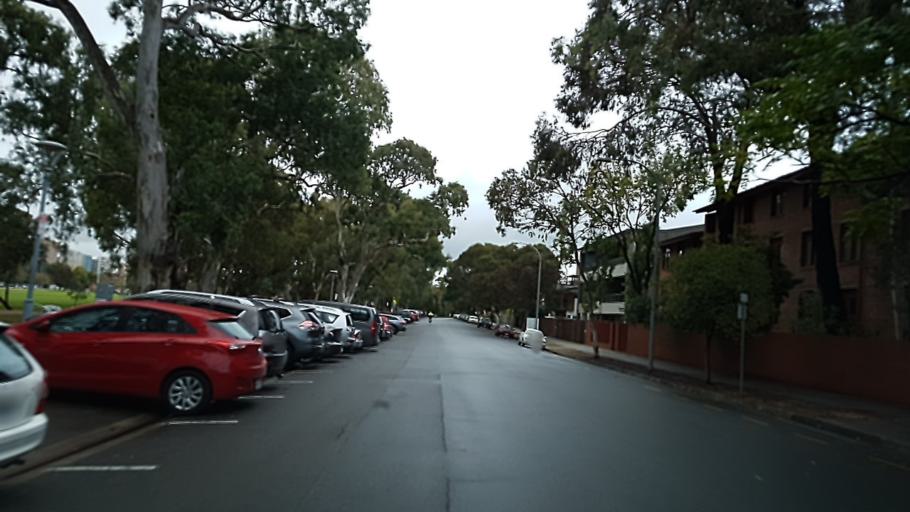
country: AU
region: South Australia
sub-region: Adelaide
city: North Adelaide
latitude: -34.9103
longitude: 138.6058
